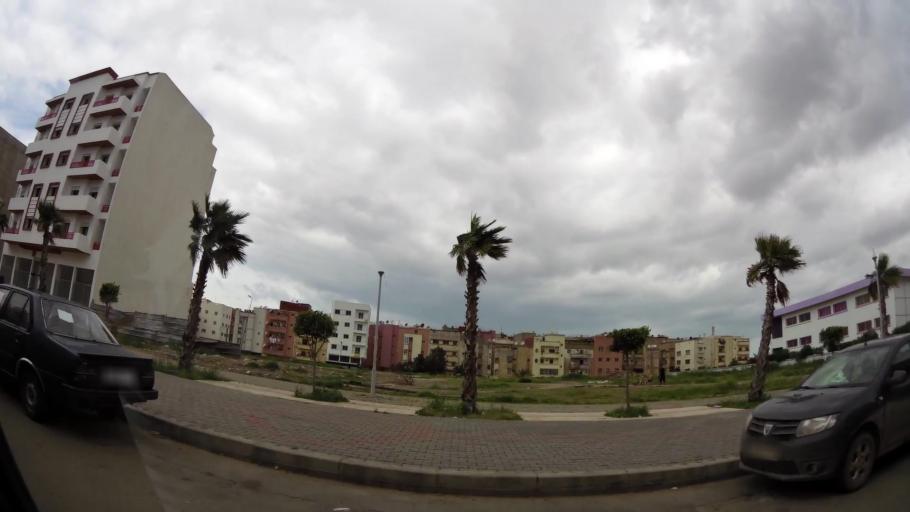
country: MA
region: Grand Casablanca
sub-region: Mediouna
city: Tit Mellil
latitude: 33.5677
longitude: -7.5496
